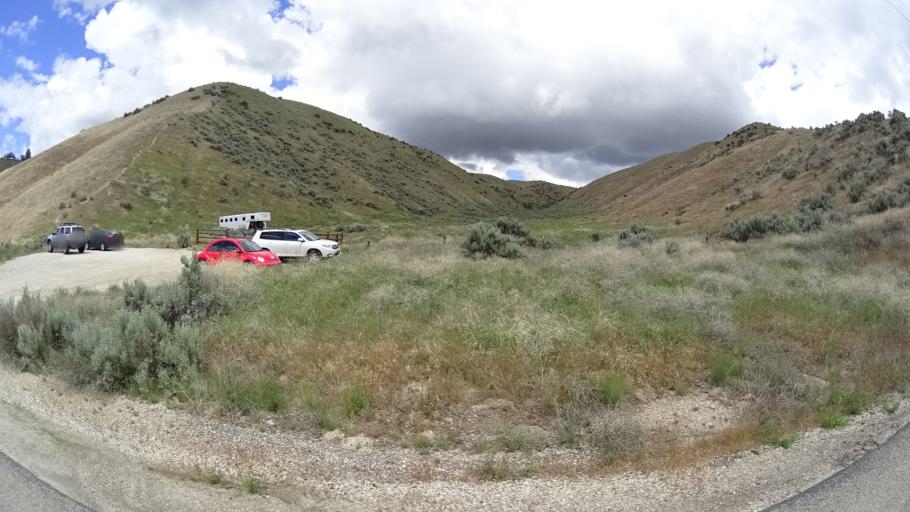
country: US
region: Idaho
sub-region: Ada County
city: Garden City
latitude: 43.6616
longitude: -116.2262
